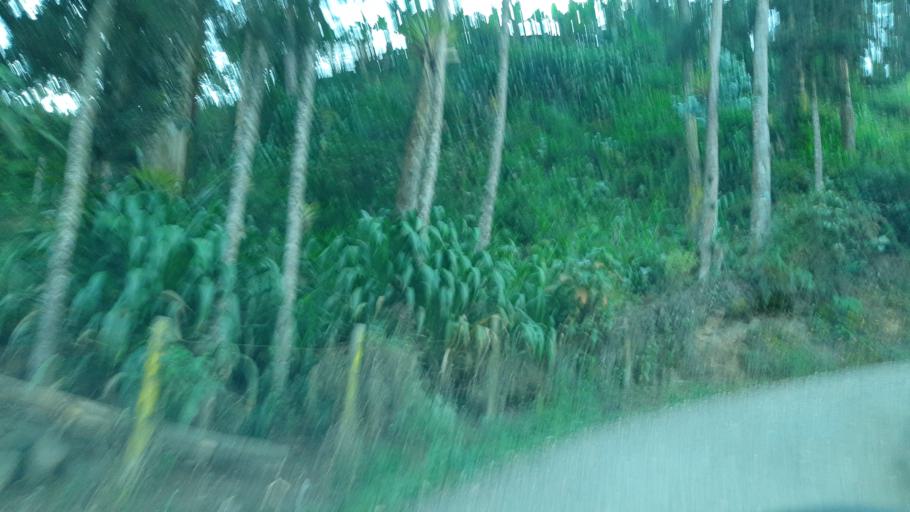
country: CO
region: Boyaca
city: Garagoa
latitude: 5.1120
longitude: -73.3510
